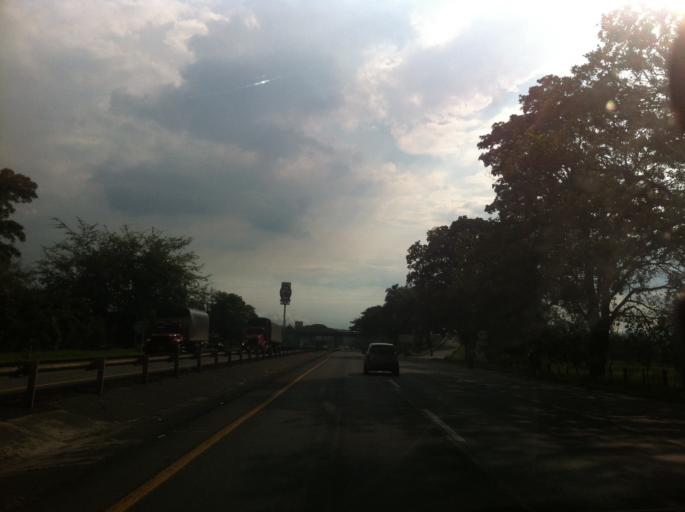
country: CO
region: Valle del Cauca
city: San Pedro
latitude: 3.9980
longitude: -76.2306
